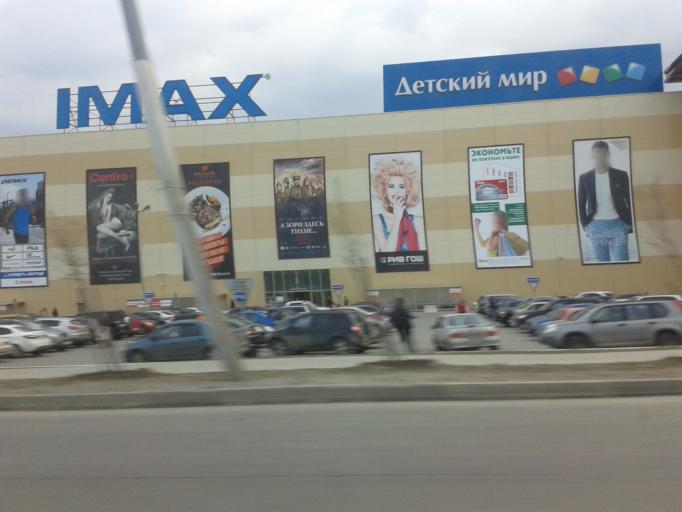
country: RU
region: Rjazan
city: Ryazan'
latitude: 54.6355
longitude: 39.6898
